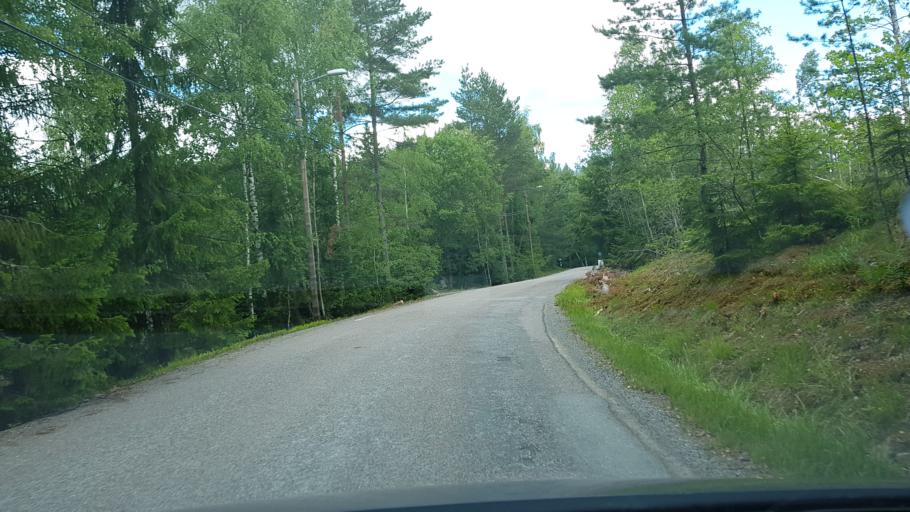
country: SE
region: Stockholm
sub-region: Upplands-Bro Kommun
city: Kungsaengen
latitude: 59.5006
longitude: 17.8096
